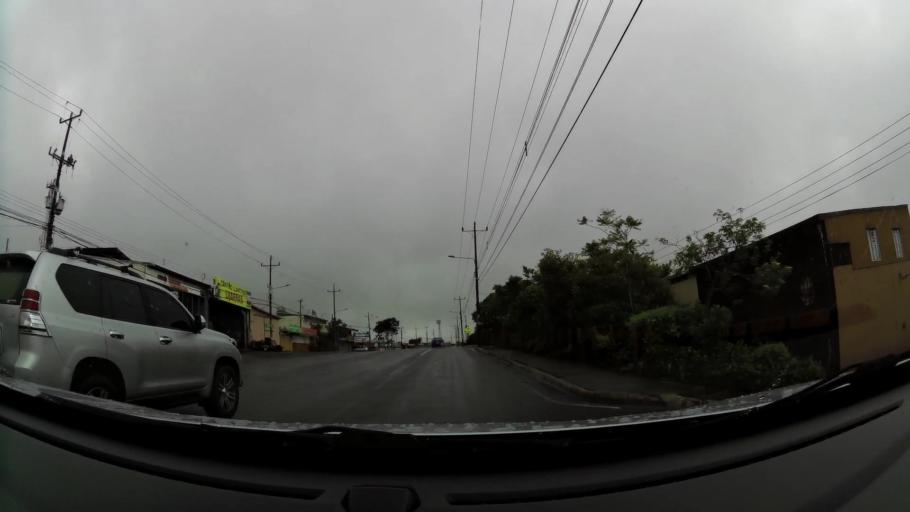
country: CR
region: Cartago
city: Paraiso
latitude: 9.8430
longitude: -83.8826
